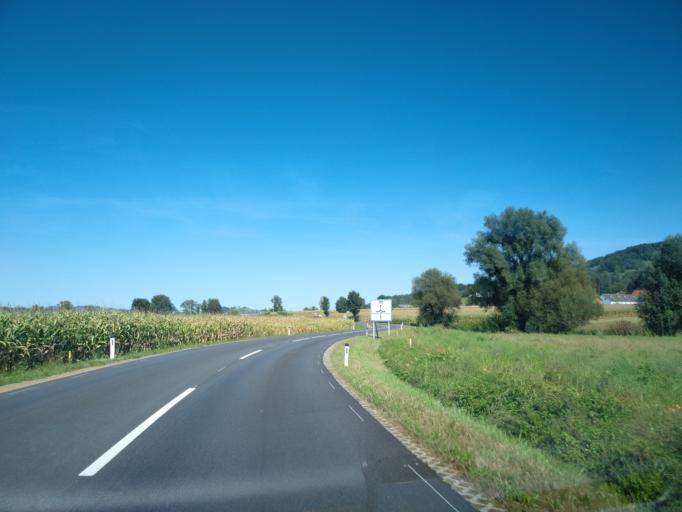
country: AT
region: Styria
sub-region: Politischer Bezirk Leibnitz
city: Sankt Johann im Saggautal
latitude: 46.7171
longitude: 15.4066
